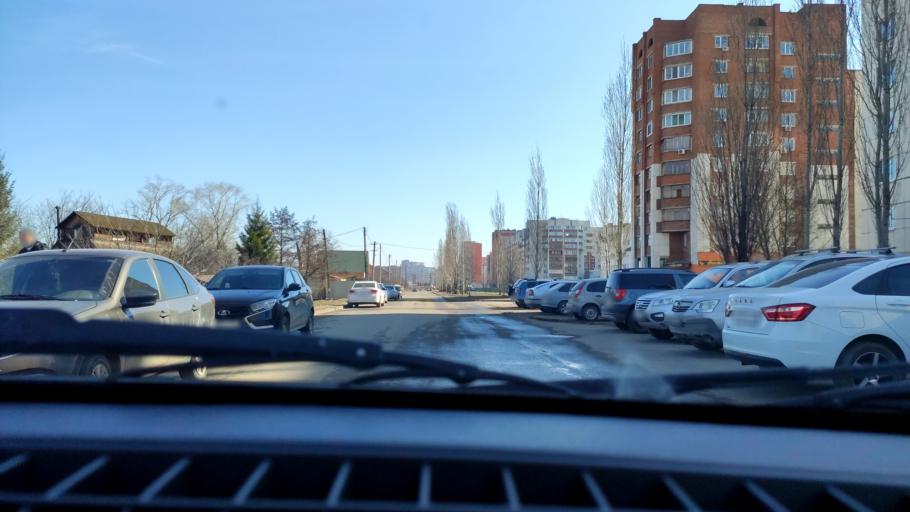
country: RU
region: Bashkortostan
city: Mikhaylovka
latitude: 54.7143
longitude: 55.8243
